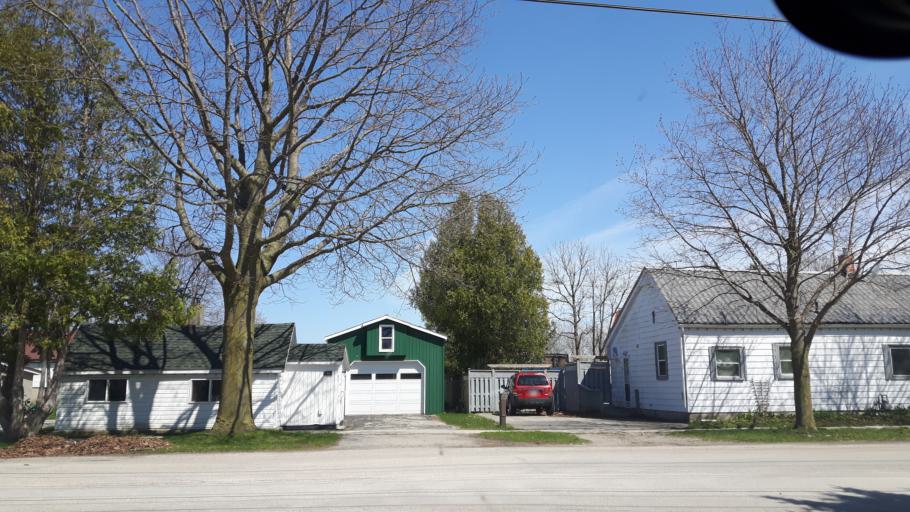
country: CA
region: Ontario
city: Goderich
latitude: 43.7464
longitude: -81.7024
